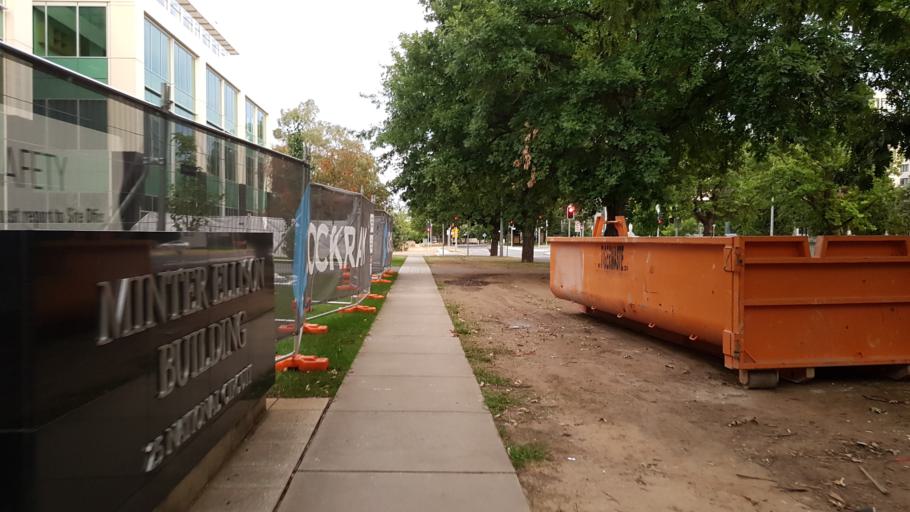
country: AU
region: Australian Capital Territory
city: Forrest
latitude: -35.3133
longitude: 149.1312
